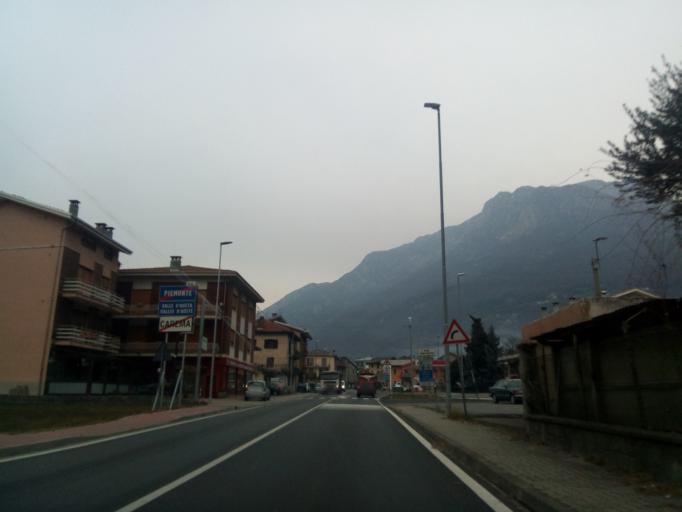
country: IT
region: Piedmont
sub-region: Provincia di Torino
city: Carema
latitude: 45.5872
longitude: 7.8026
